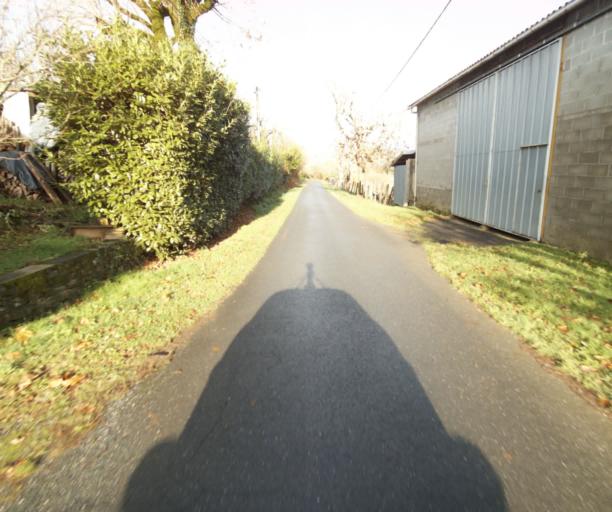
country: FR
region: Limousin
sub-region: Departement de la Correze
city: Saint-Mexant
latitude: 45.2547
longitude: 1.6267
